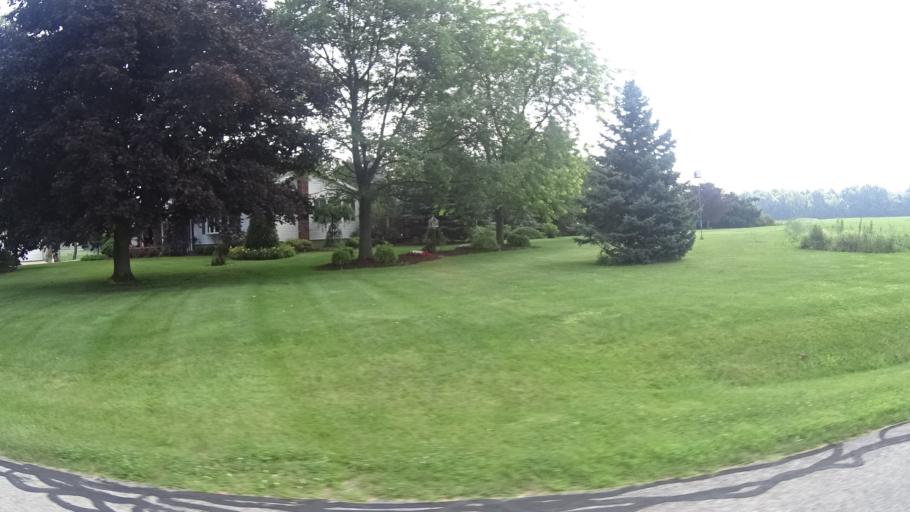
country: US
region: Ohio
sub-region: Huron County
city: Wakeman
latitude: 41.2982
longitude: -82.4565
